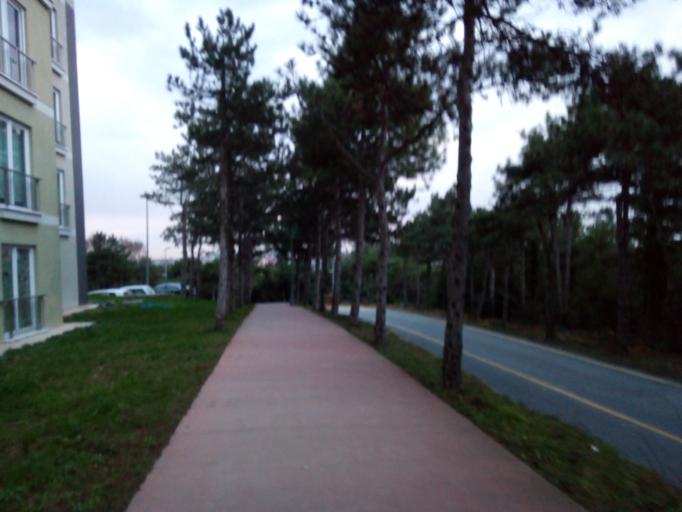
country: TR
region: Istanbul
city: Sisli
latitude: 41.1057
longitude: 29.0303
